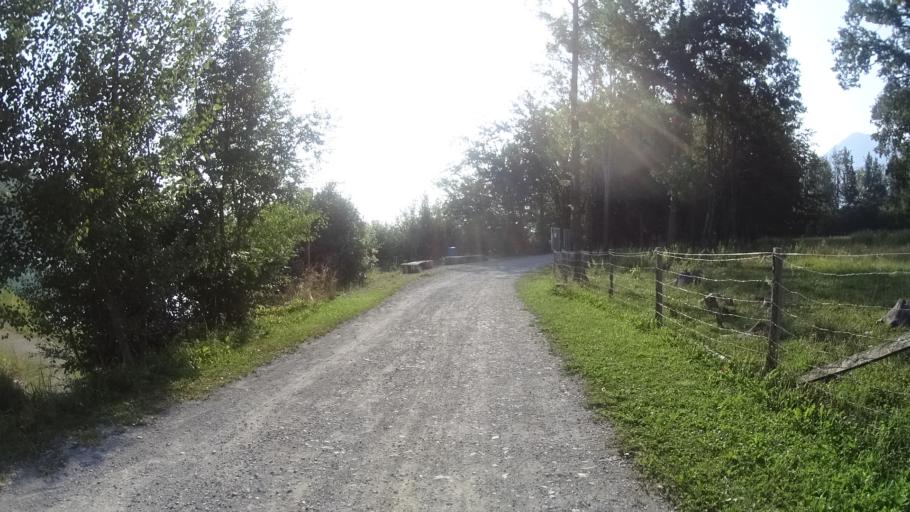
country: AT
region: Carinthia
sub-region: Politischer Bezirk Klagenfurt Land
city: Ludmannsdorf
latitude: 46.5327
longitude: 14.1366
